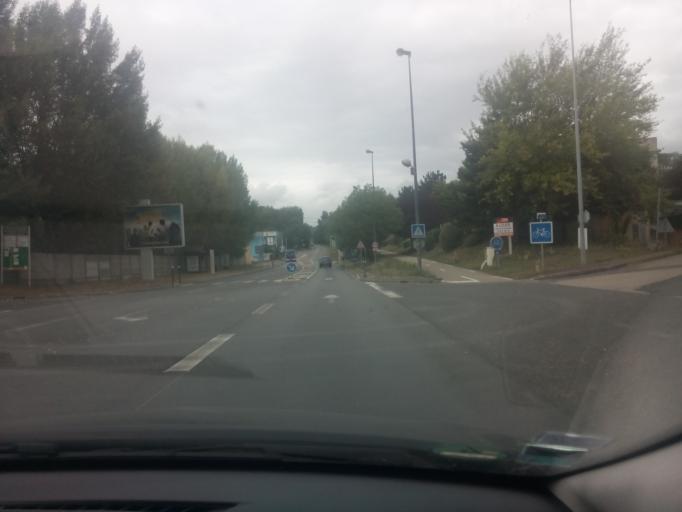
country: FR
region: Ile-de-France
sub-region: Departement de l'Essonne
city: Saulx-les-Chartreux
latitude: 48.6997
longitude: 2.2671
